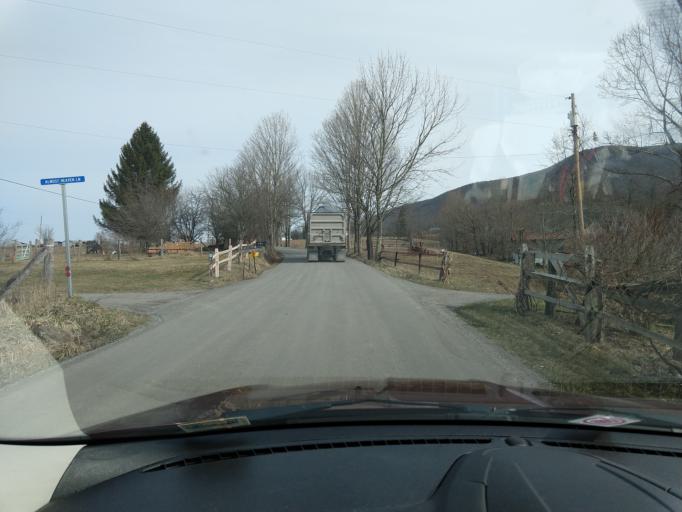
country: US
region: West Virginia
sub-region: Tucker County
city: Parsons
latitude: 39.0148
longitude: -79.5112
